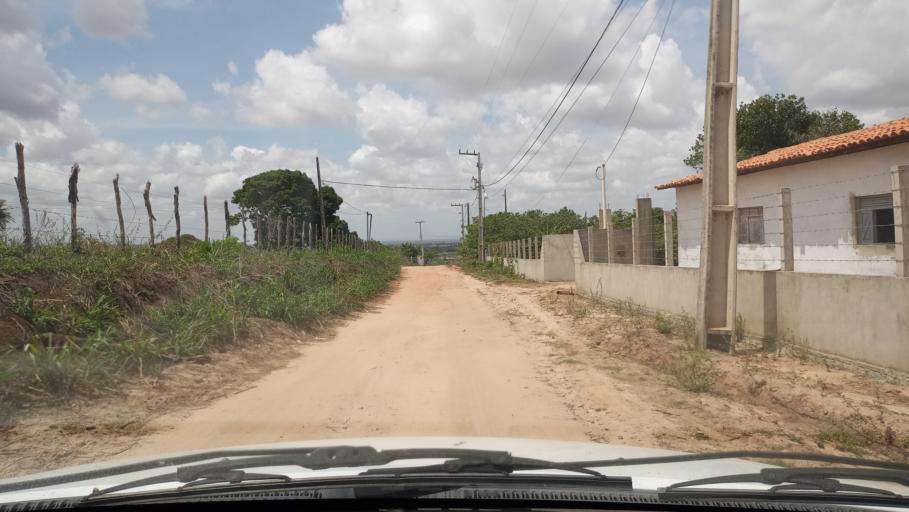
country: BR
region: Rio Grande do Norte
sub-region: Brejinho
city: Brejinho
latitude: -6.2641
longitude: -35.3425
